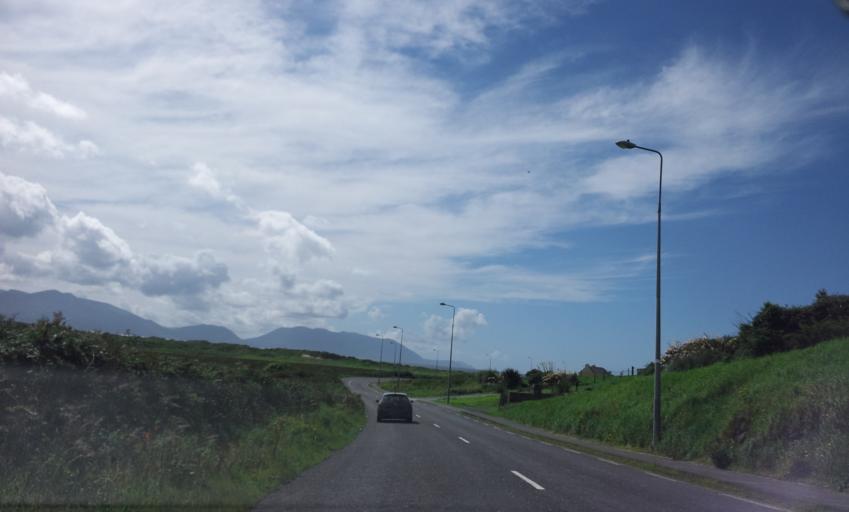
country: IE
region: Munster
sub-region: Ciarrai
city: Killorglin
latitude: 52.1459
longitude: -9.9726
